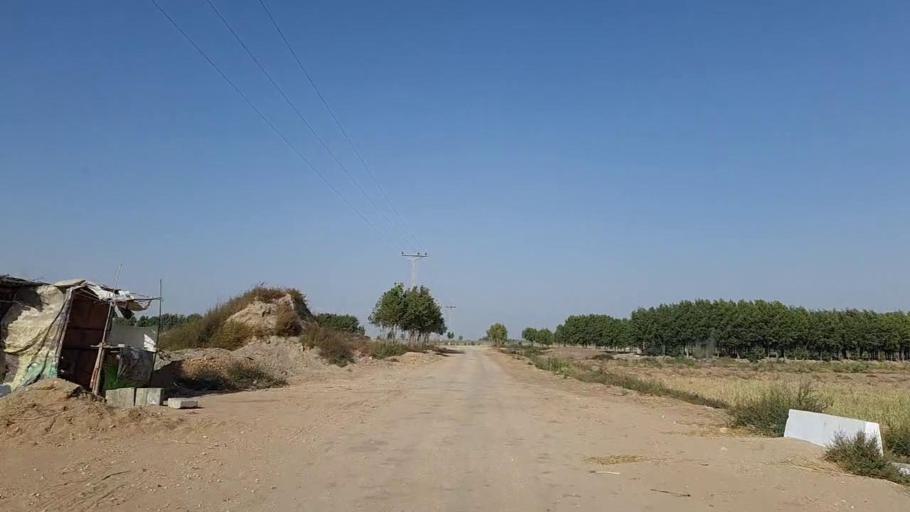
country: PK
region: Sindh
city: Jati
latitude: 24.5135
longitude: 68.1752
